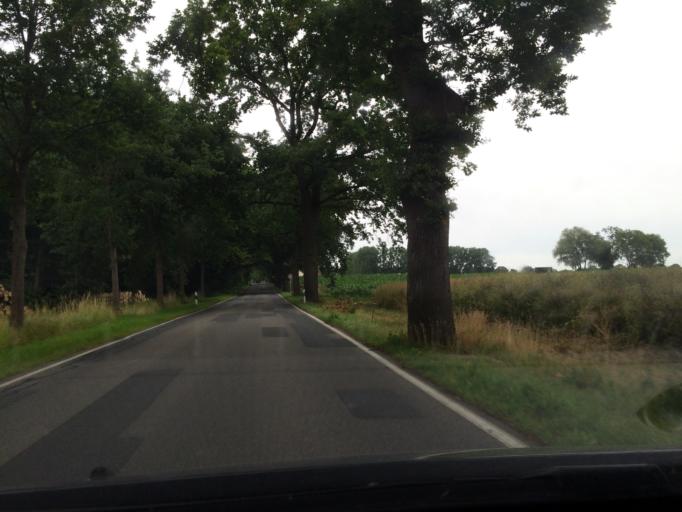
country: DE
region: Mecklenburg-Vorpommern
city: Prohn
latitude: 54.3975
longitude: 13.0090
